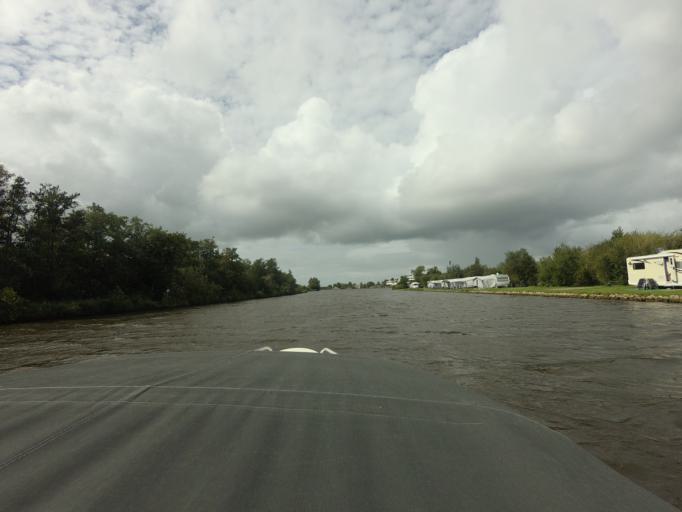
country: NL
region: Friesland
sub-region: Gemeente Boarnsterhim
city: Warten
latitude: 53.1261
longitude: 5.9373
